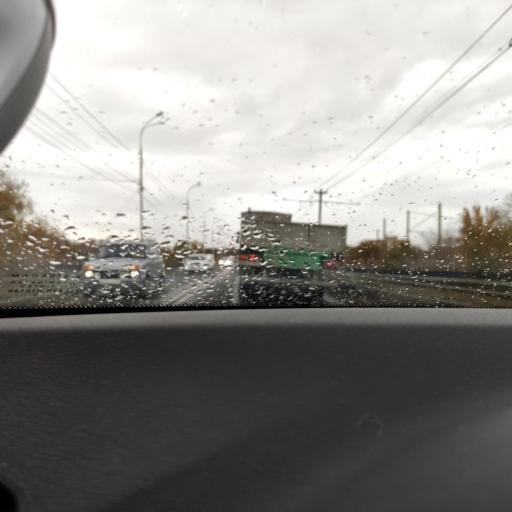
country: RU
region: Samara
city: Smyshlyayevka
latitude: 53.2197
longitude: 50.2901
